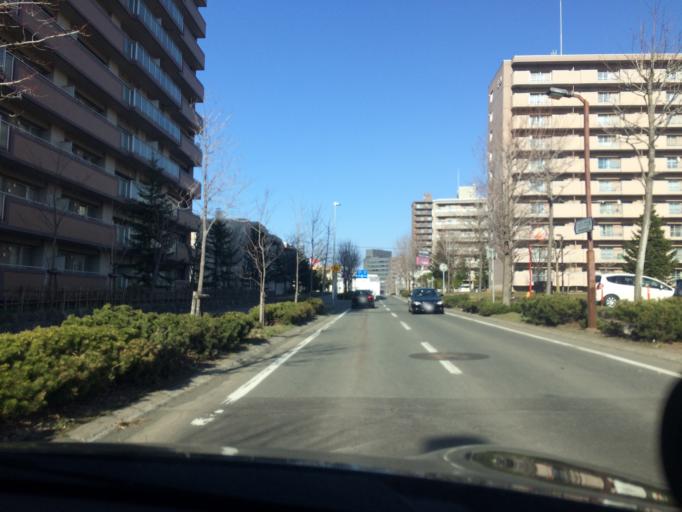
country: JP
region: Hokkaido
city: Ebetsu
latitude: 43.0352
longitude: 141.4677
